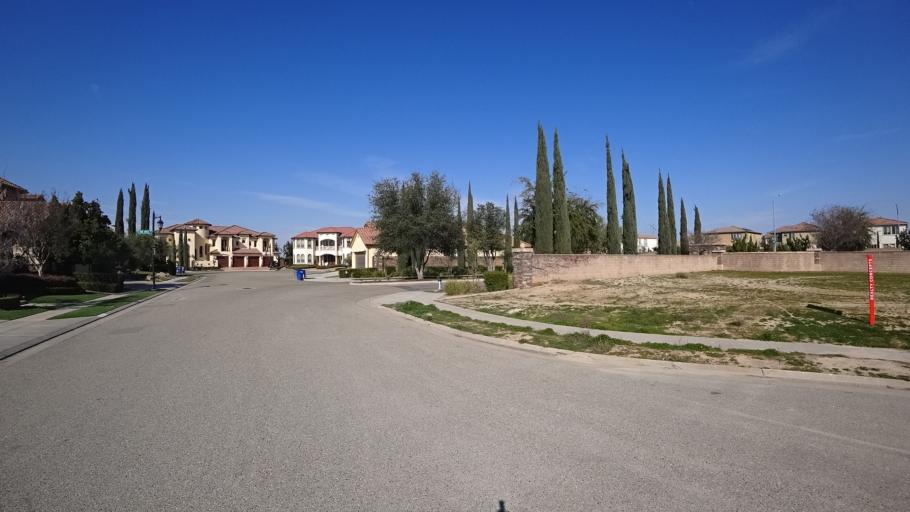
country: US
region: California
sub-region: Fresno County
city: Clovis
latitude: 36.8943
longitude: -119.7482
